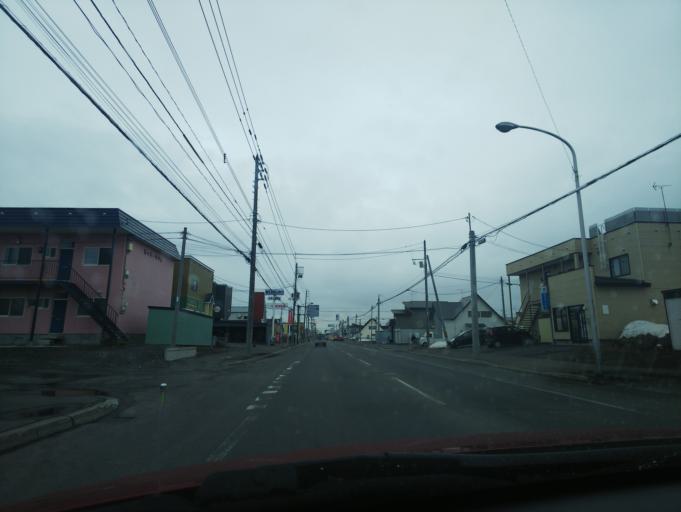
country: JP
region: Hokkaido
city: Nayoro
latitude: 44.3527
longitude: 142.4503
